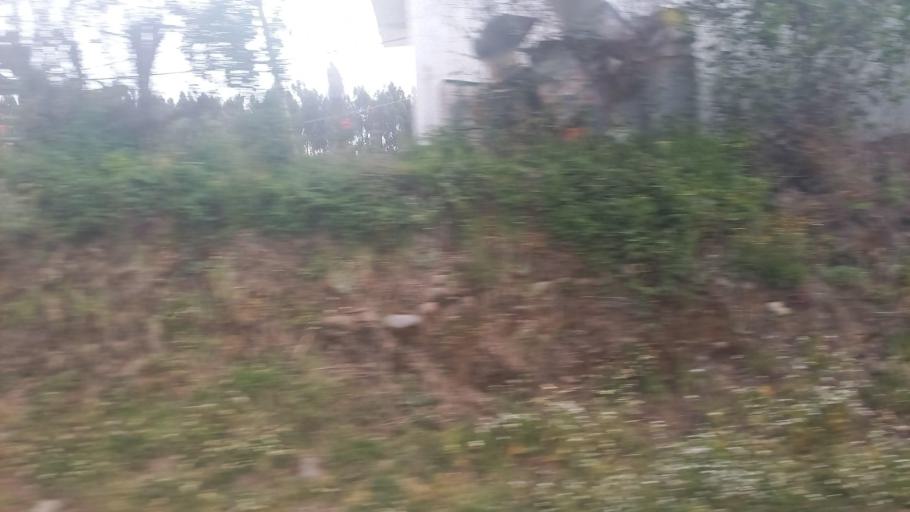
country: EC
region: Pichincha
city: Cayambe
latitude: 0.0913
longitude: -78.0979
